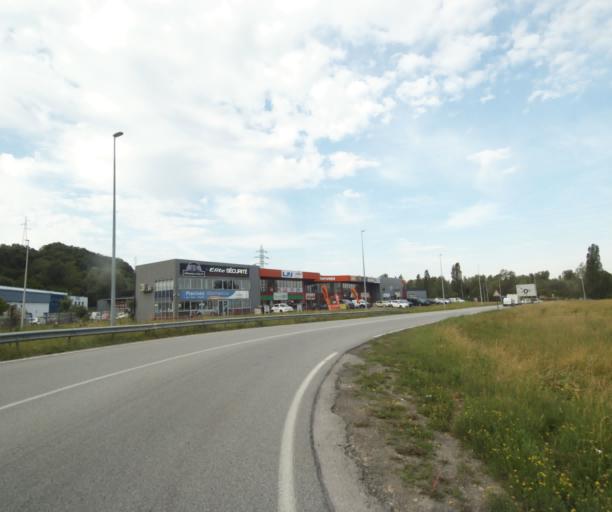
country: FR
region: Rhone-Alpes
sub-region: Departement de la Haute-Savoie
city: Marin
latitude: 46.3807
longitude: 6.5104
